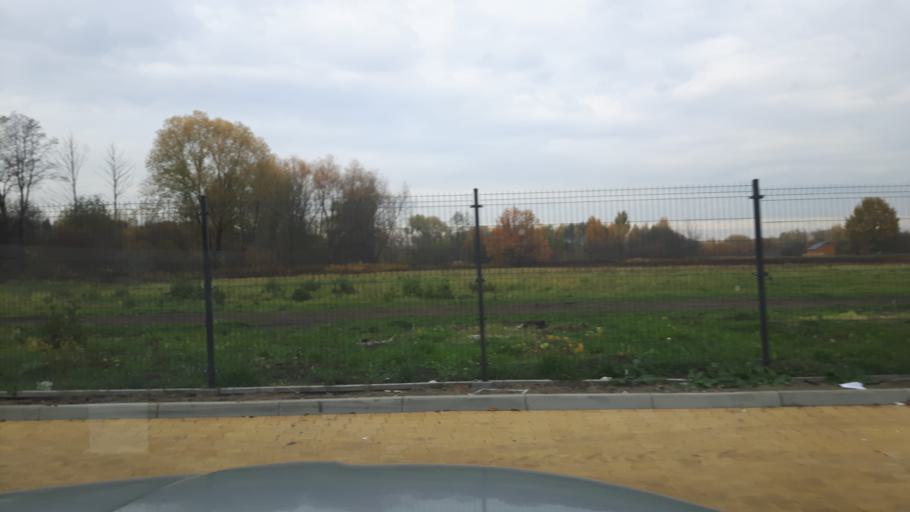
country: PL
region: Masovian Voivodeship
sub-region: Warszawa
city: Ursynow
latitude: 52.1571
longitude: 21.0630
